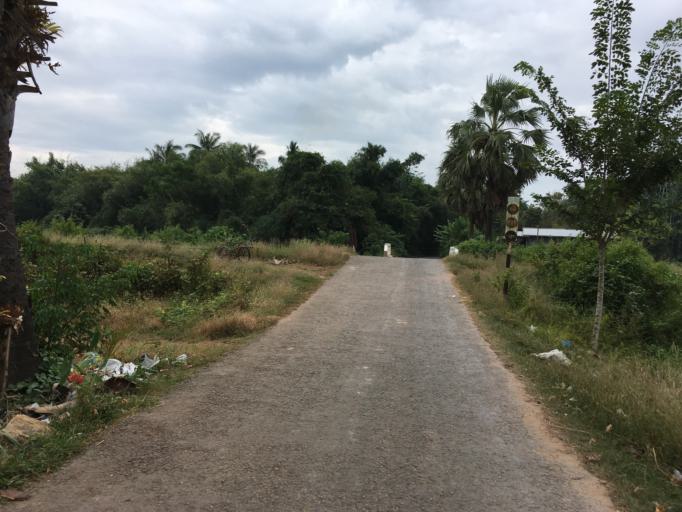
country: MM
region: Mon
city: Mawlamyine
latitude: 16.4337
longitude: 97.6295
